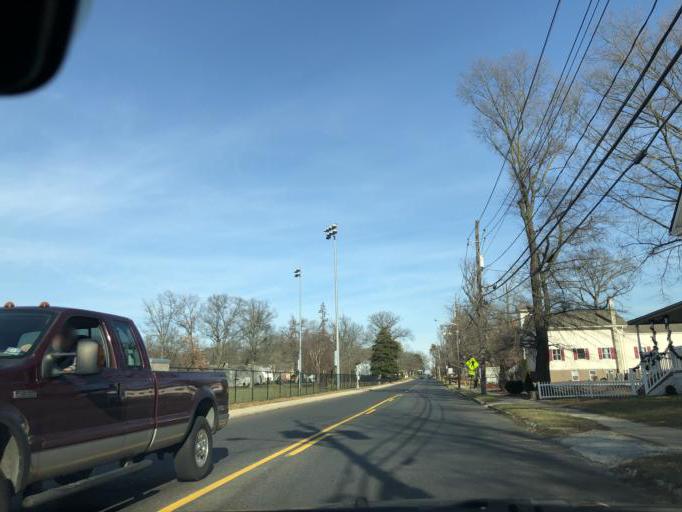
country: US
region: New Jersey
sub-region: Burlington County
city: Maple Shade
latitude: 39.9593
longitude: -74.9794
